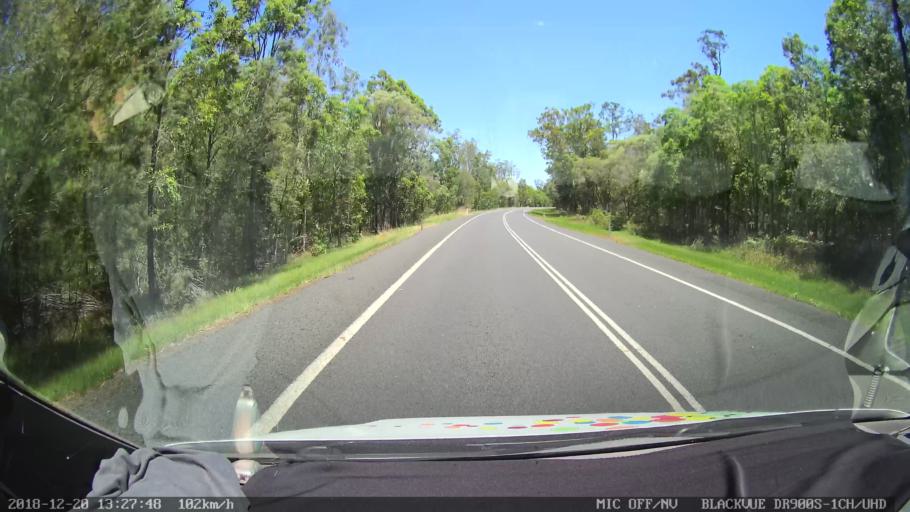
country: AU
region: New South Wales
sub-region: Clarence Valley
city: Gordon
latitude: -29.1653
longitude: 152.9931
